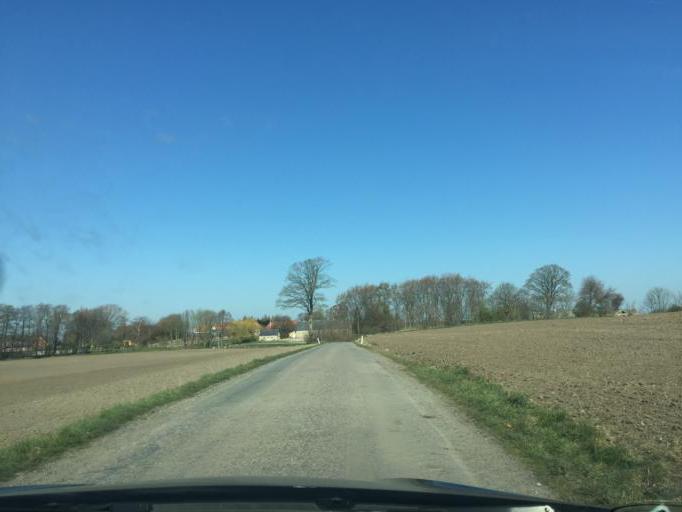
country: DK
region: South Denmark
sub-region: Faaborg-Midtfyn Kommune
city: Arslev
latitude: 55.2941
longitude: 10.5203
